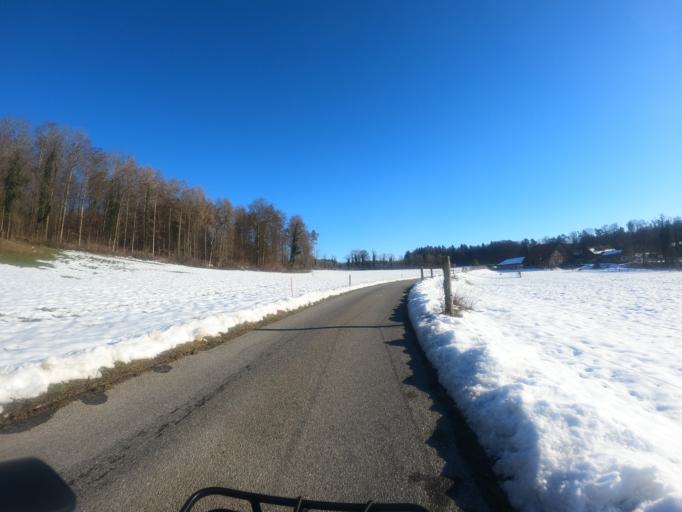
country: CH
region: Aargau
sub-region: Bezirk Bremgarten
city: Oberlunkhofen
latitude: 47.3226
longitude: 8.3945
